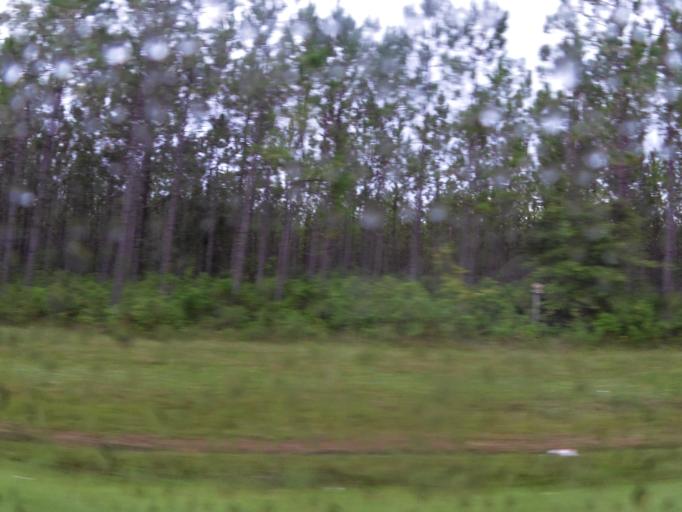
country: US
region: Florida
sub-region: Nassau County
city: Callahan
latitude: 30.5124
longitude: -81.9939
